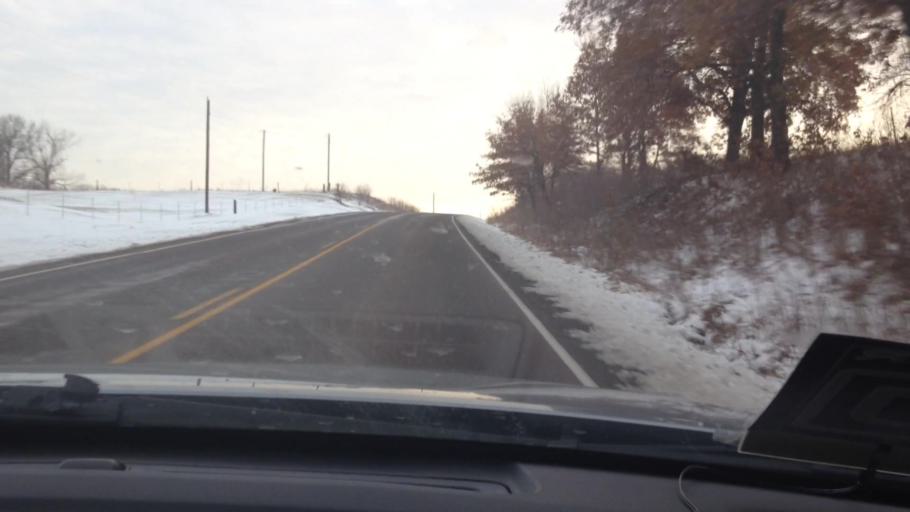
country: US
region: Kansas
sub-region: Leavenworth County
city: Leavenworth
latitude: 39.2585
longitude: -94.9725
